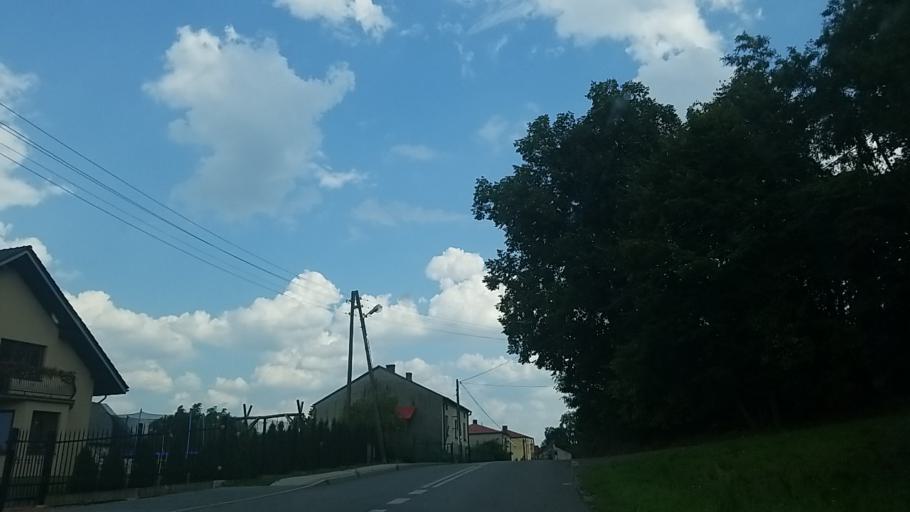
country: PL
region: Lublin Voivodeship
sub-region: Powiat bilgorajski
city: Goraj
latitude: 50.7237
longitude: 22.6592
